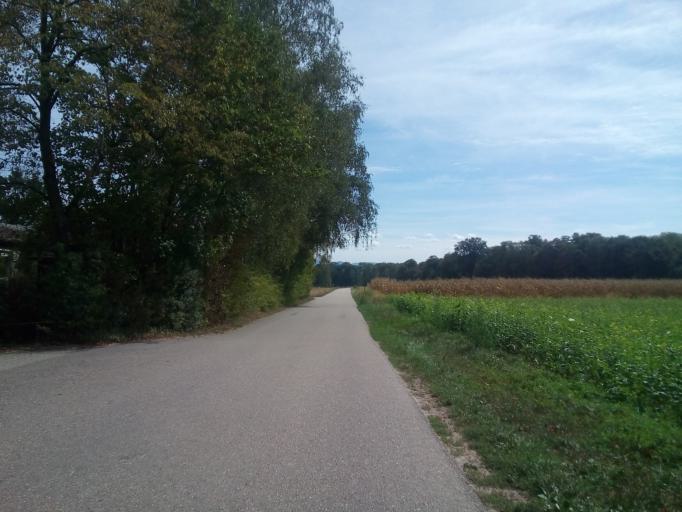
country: DE
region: Baden-Wuerttemberg
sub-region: Karlsruhe Region
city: Lichtenau
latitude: 48.7060
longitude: 8.0116
